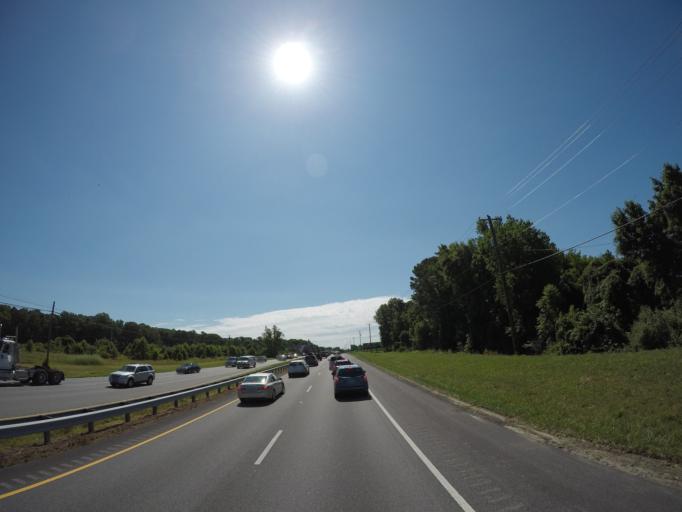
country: US
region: Maryland
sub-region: Queen Anne's County
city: Grasonville
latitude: 38.9788
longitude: -76.1373
